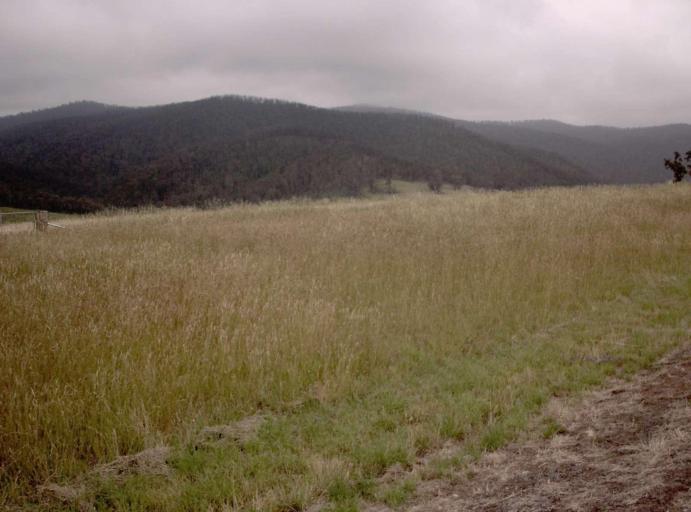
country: AU
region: Victoria
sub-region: Wellington
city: Heyfield
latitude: -37.8366
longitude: 146.6827
